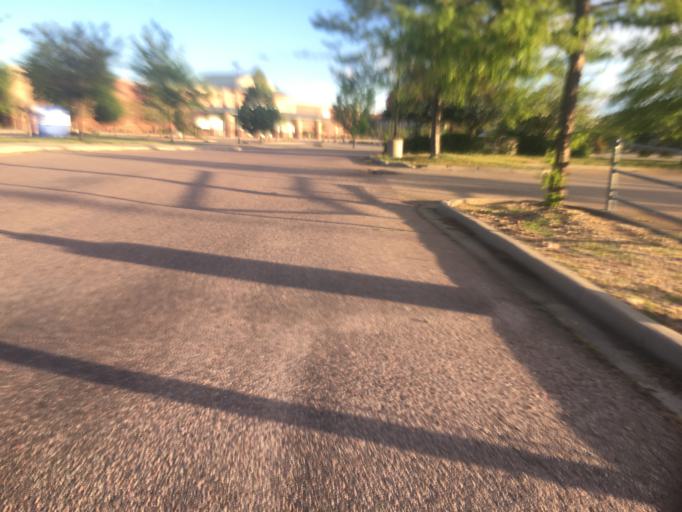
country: US
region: Colorado
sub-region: Boulder County
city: Superior
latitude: 39.9619
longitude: -105.1610
